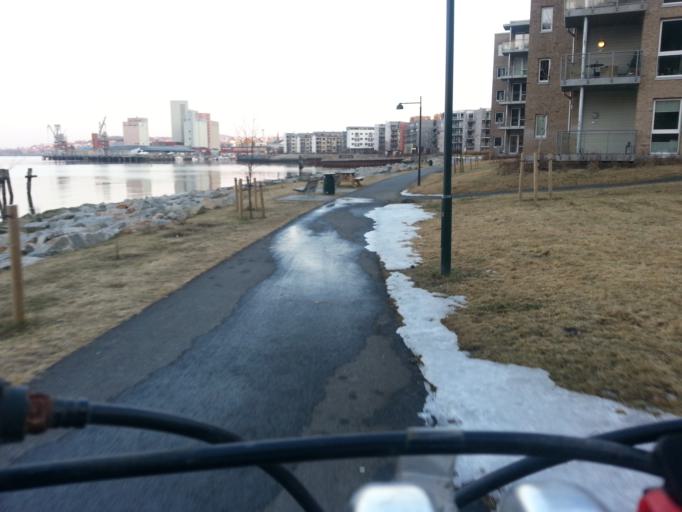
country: NO
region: Sor-Trondelag
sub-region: Trondheim
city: Trondheim
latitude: 63.4336
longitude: 10.3516
